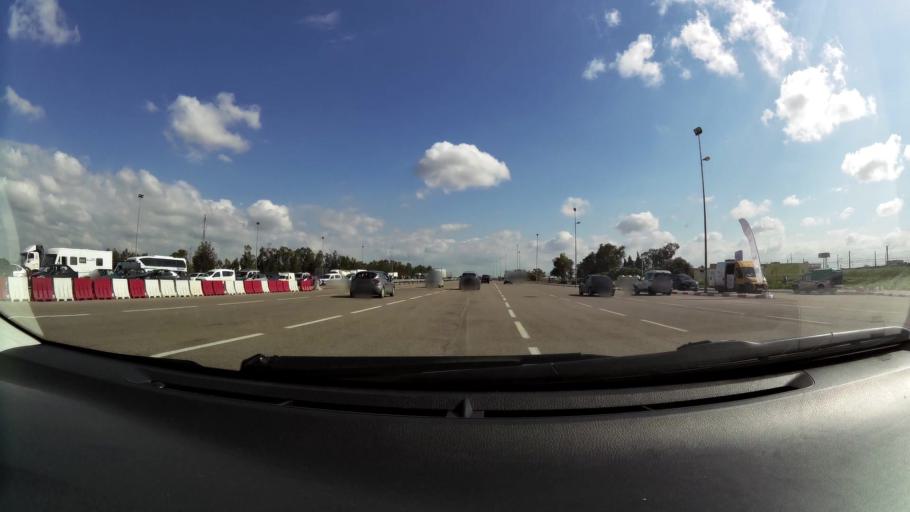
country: MA
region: Chaouia-Ouardigha
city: Nouaseur
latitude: 33.3674
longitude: -7.6204
